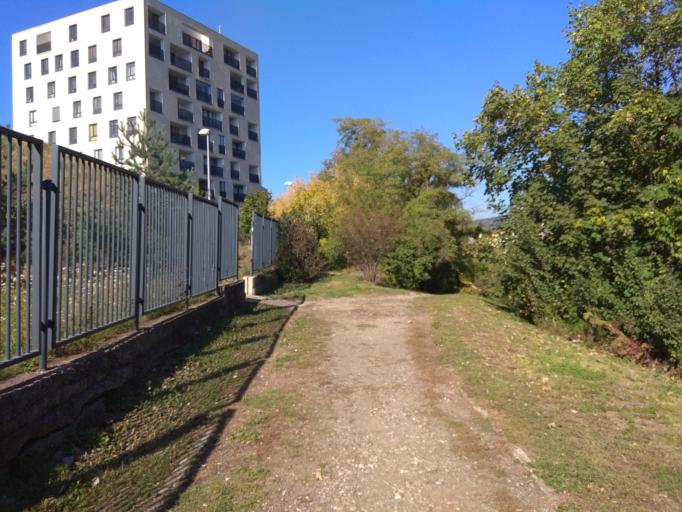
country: SK
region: Kosicky
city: Kosice
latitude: 48.7232
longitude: 21.2422
